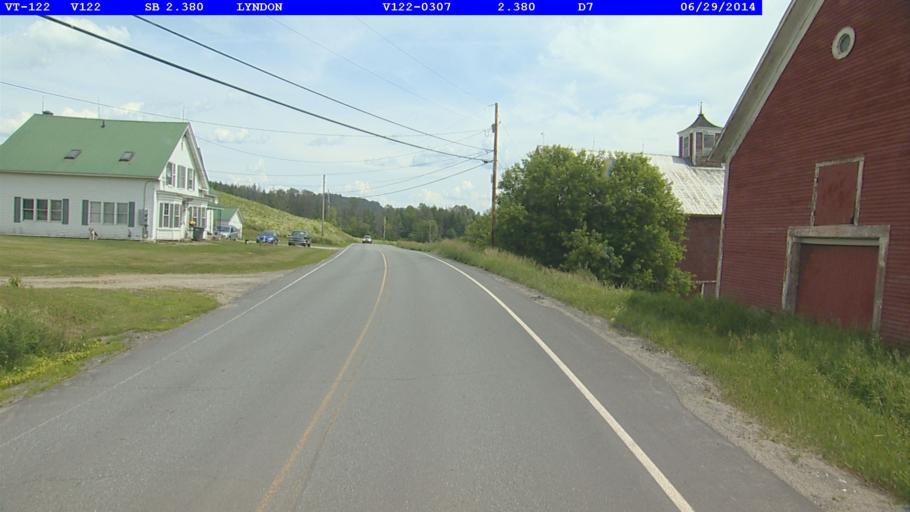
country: US
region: Vermont
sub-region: Caledonia County
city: Lyndonville
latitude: 44.5601
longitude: -72.0358
